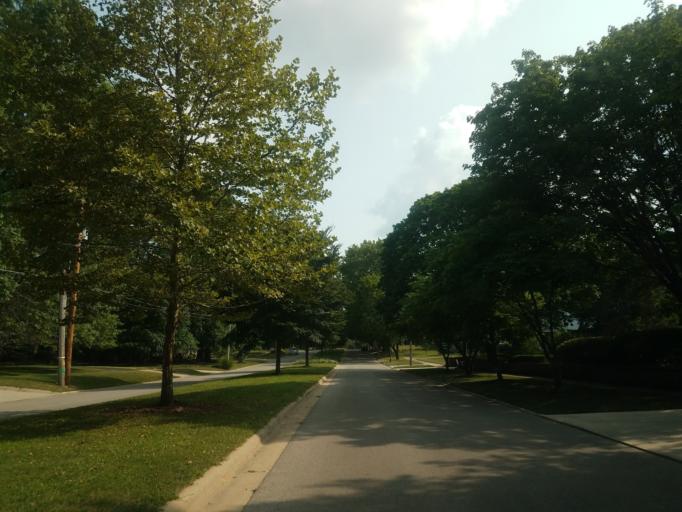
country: US
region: Illinois
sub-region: McLean County
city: Normal
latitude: 40.5003
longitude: -88.9856
